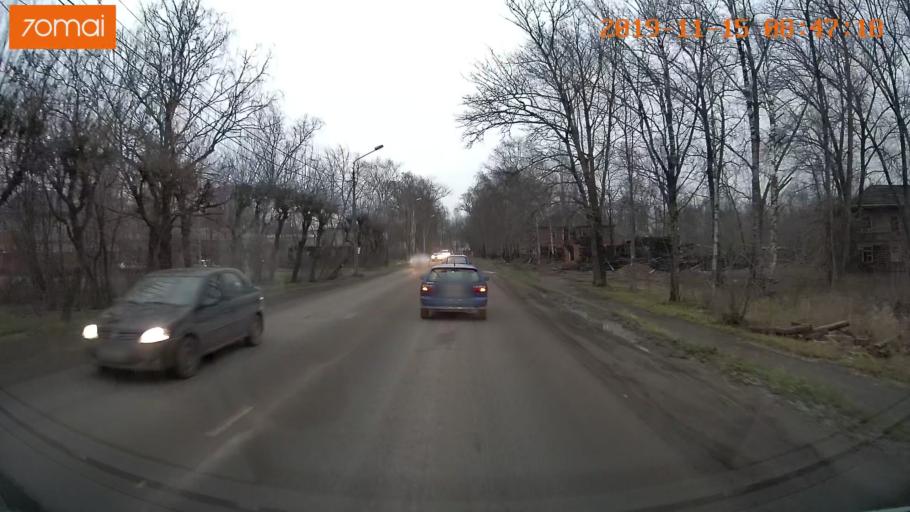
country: RU
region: Vologda
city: Cherepovets
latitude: 59.1204
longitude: 37.9144
